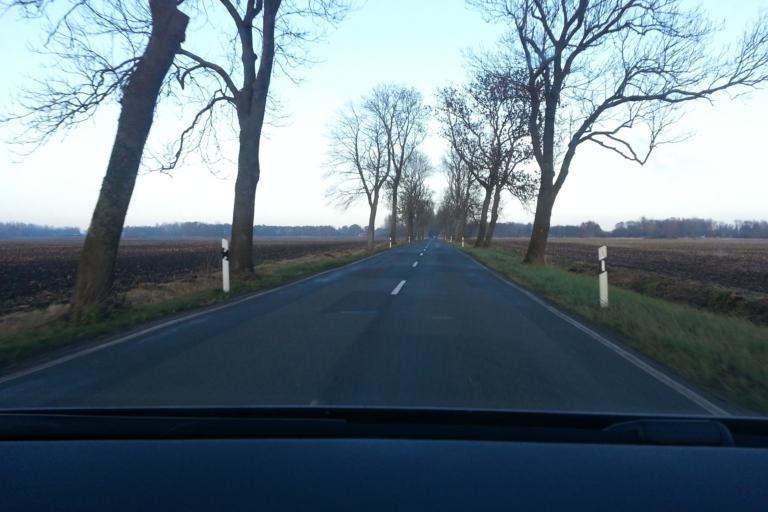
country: DE
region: Mecklenburg-Vorpommern
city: Ferdinandshof
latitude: 53.6487
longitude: 13.8665
